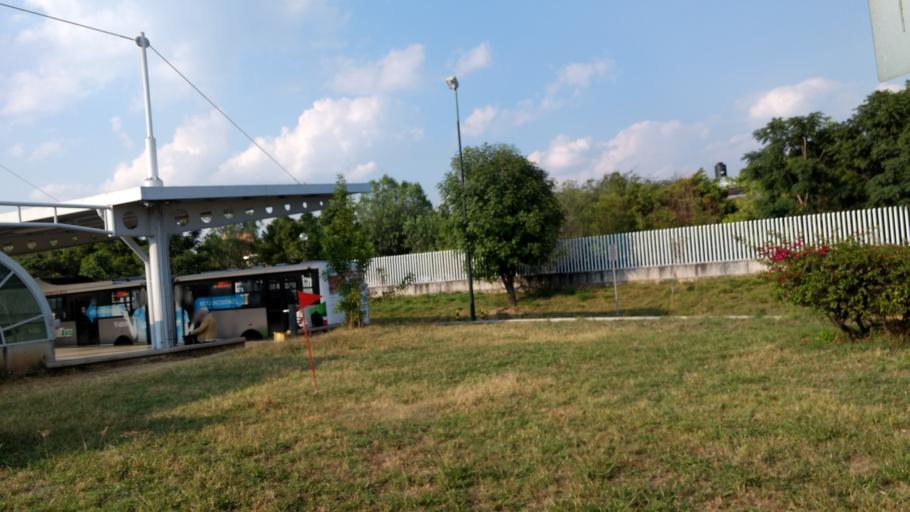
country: MX
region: Guanajuato
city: Leon
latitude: 21.1497
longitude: -101.6743
